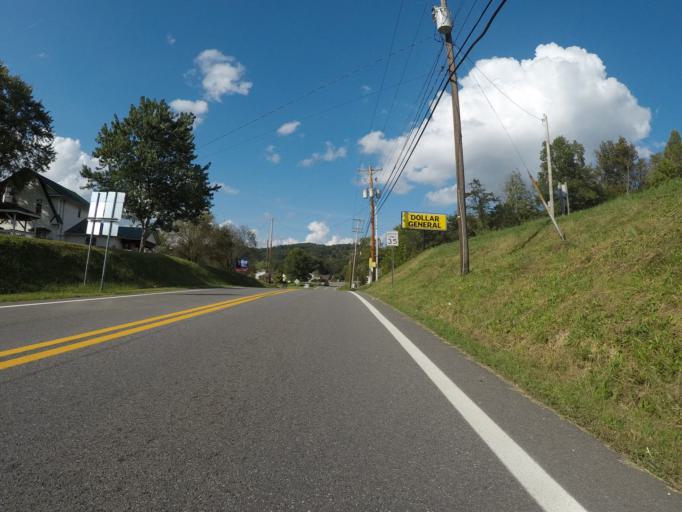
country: US
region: Ohio
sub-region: Lawrence County
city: Burlington
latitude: 38.3549
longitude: -82.5046
